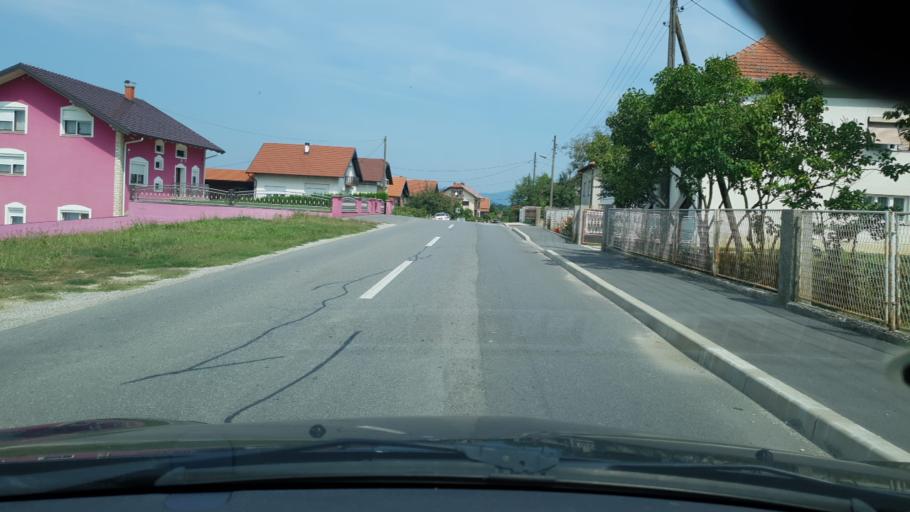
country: HR
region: Krapinsko-Zagorska
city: Marija Bistrica
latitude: 46.0278
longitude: 16.0998
